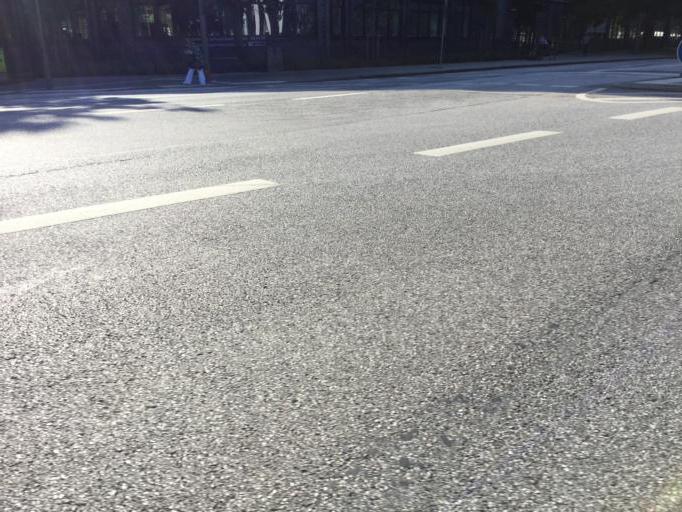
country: DE
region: Hamburg
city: Langenhorn
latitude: 53.6760
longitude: 10.0015
